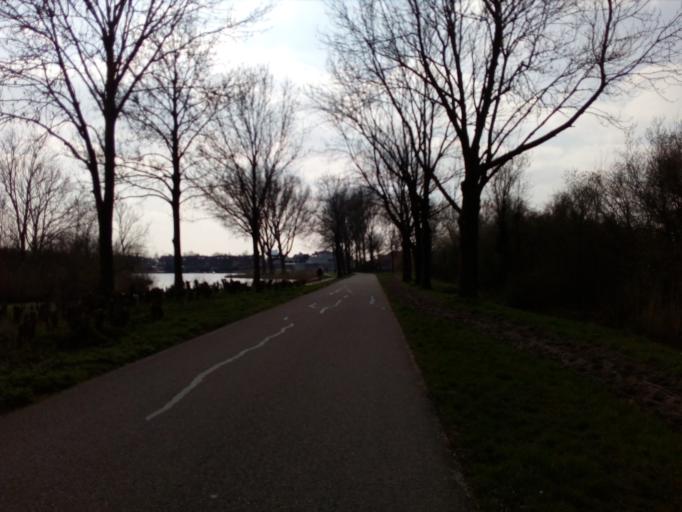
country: NL
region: South Holland
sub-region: Gemeente Zoetermeer
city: Zoetermeer
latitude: 52.0804
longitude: 4.4992
